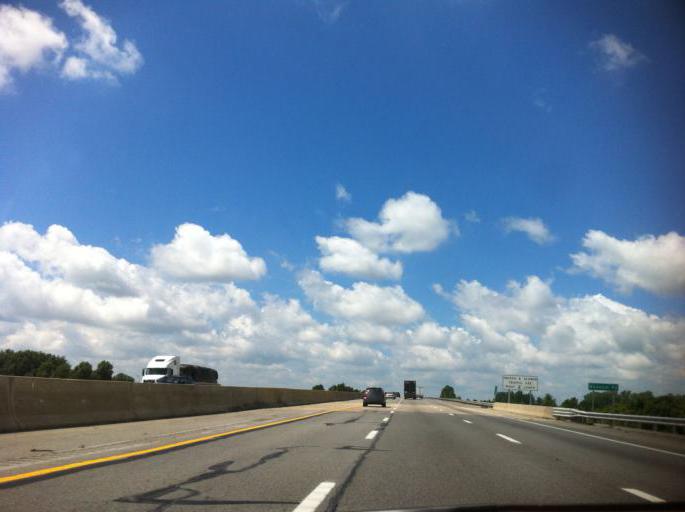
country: US
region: Ohio
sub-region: Huron County
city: Monroeville
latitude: 41.3357
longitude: -82.6926
